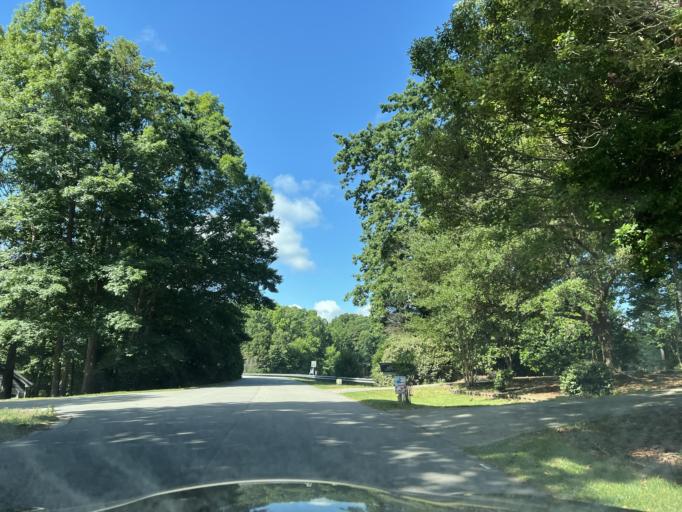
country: US
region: North Carolina
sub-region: Wake County
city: Wake Forest
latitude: 35.9431
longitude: -78.6331
